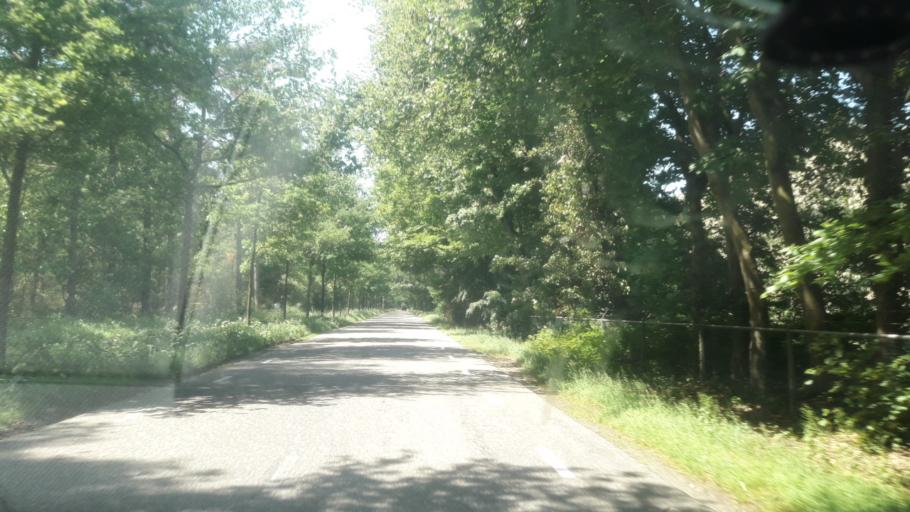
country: NL
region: Overijssel
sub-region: Gemeente Deventer
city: Schalkhaar
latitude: 52.3227
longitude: 6.1943
